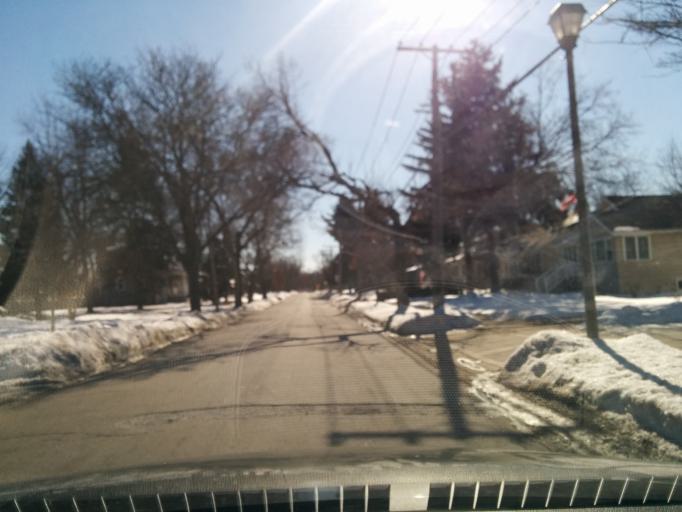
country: US
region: Illinois
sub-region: DuPage County
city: Elmhurst
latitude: 41.8895
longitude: -87.9594
